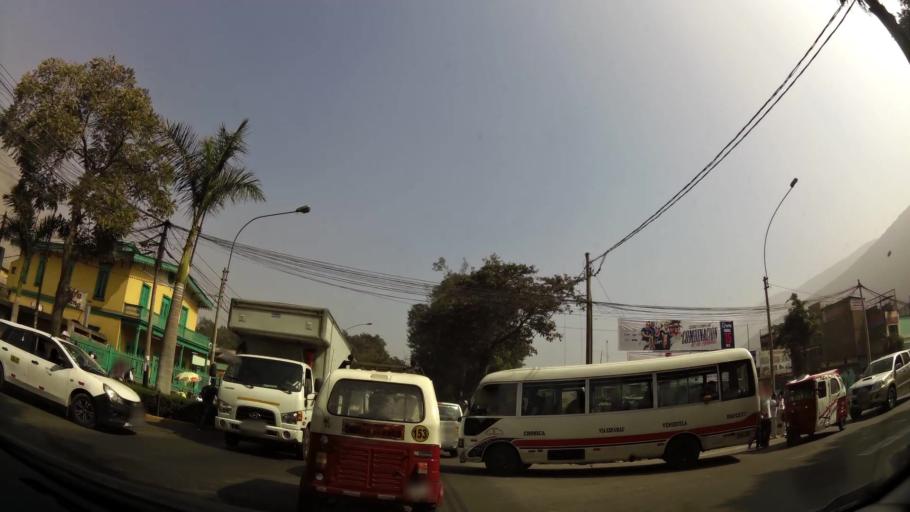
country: PE
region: Lima
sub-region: Lima
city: Asentamiento Humano Nicolas de Pierola
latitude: -11.9349
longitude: -76.6947
